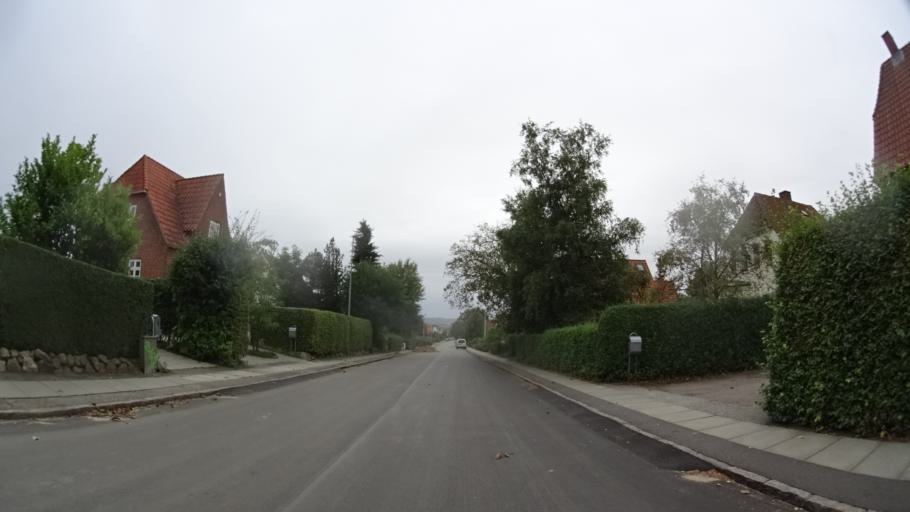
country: DK
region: Central Jutland
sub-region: Arhus Kommune
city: Stavtrup
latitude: 56.1566
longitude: 10.1466
